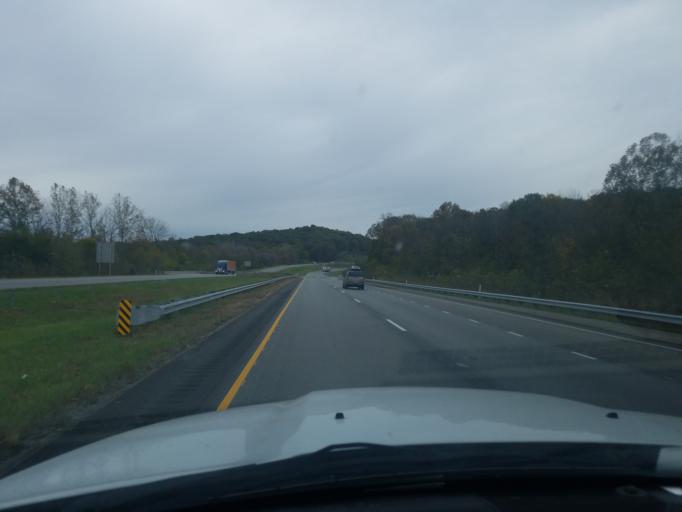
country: US
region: Indiana
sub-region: Dubois County
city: Ferdinand
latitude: 38.2273
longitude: -86.6954
